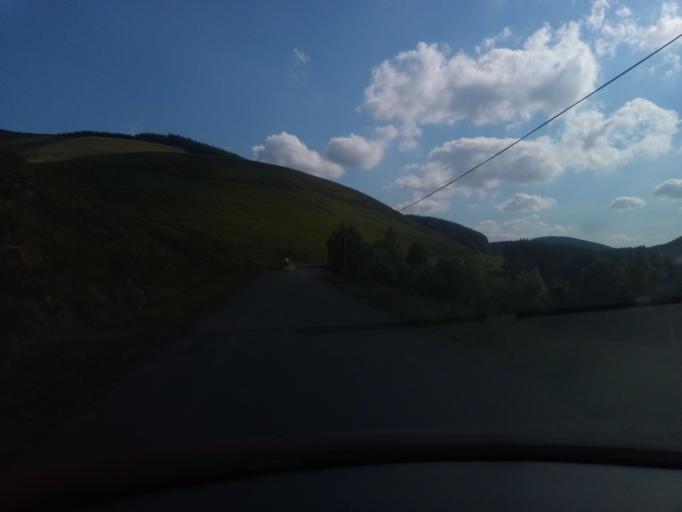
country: GB
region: Scotland
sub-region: The Scottish Borders
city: Innerleithen
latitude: 55.4818
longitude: -3.1338
